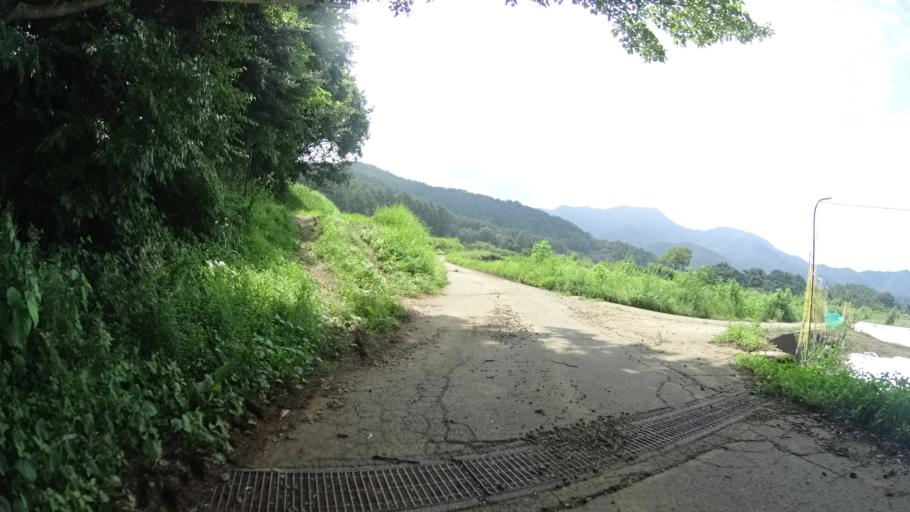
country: JP
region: Yamanashi
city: Nirasaki
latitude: 35.8981
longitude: 138.4713
